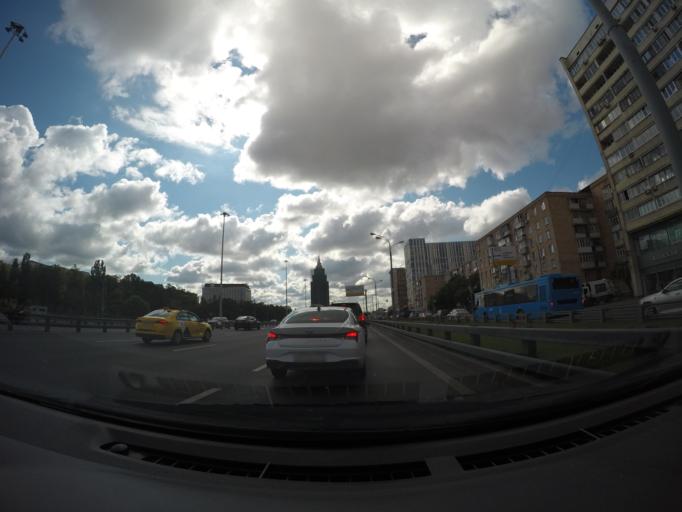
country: RU
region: Moskovskaya
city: Dorogomilovo
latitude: 55.7883
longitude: 37.5588
